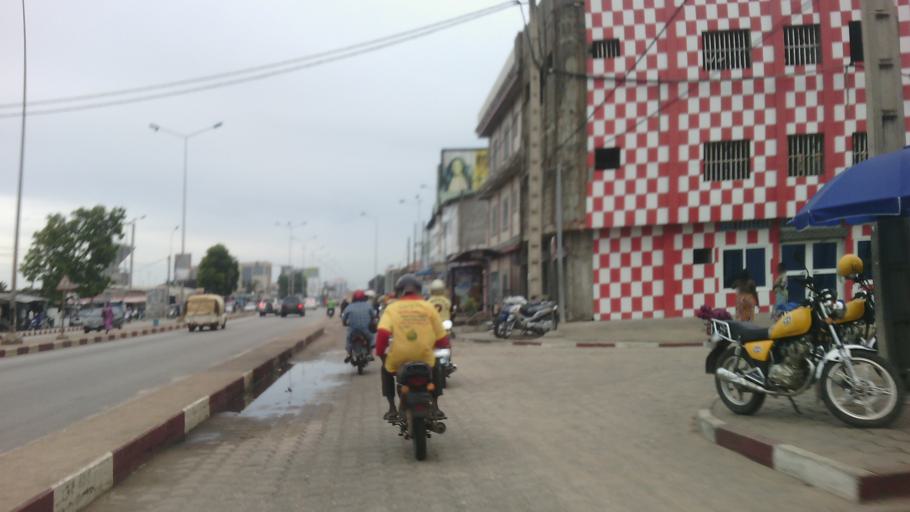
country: BJ
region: Littoral
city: Cotonou
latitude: 6.3640
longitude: 2.4184
